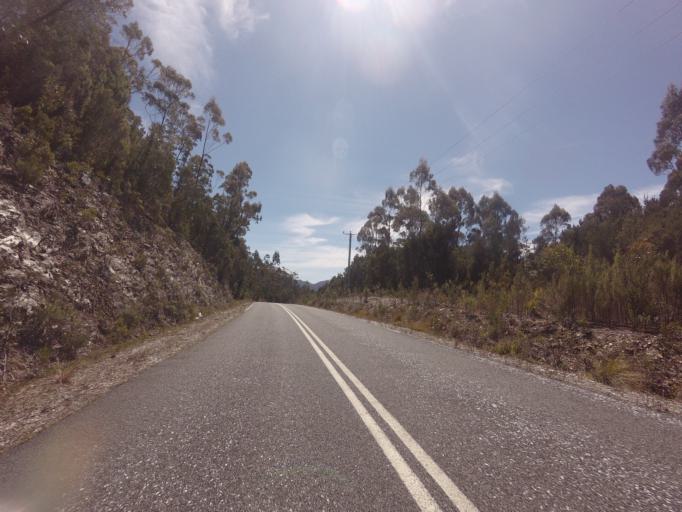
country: AU
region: Tasmania
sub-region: West Coast
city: Queenstown
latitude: -42.7634
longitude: 146.0056
